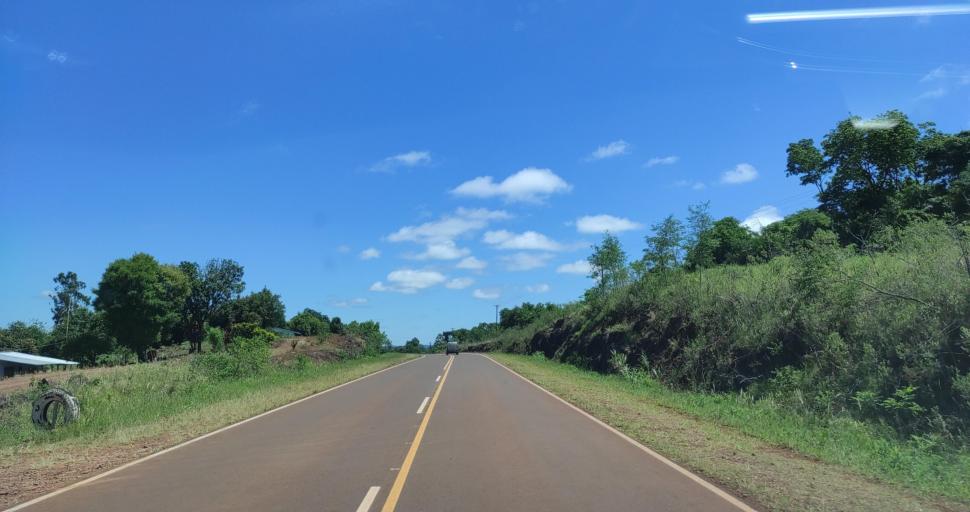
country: AR
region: Misiones
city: Campo Grande
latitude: -27.3304
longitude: -54.8899
